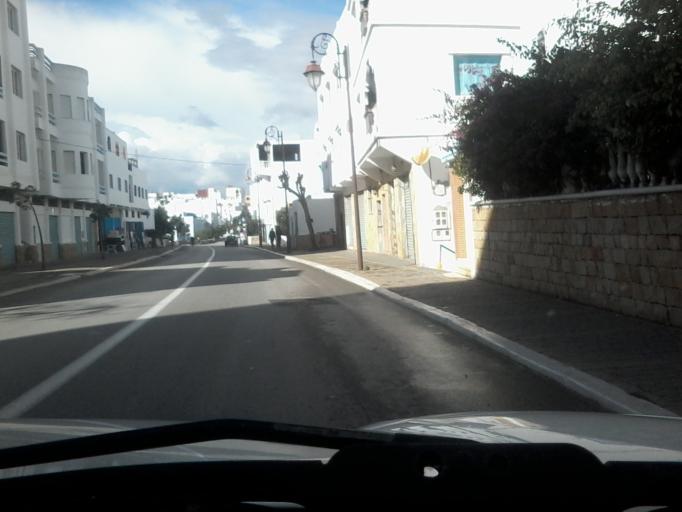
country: MA
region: Tanger-Tetouan
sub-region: Tetouan
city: Martil
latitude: 35.6792
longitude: -5.3251
